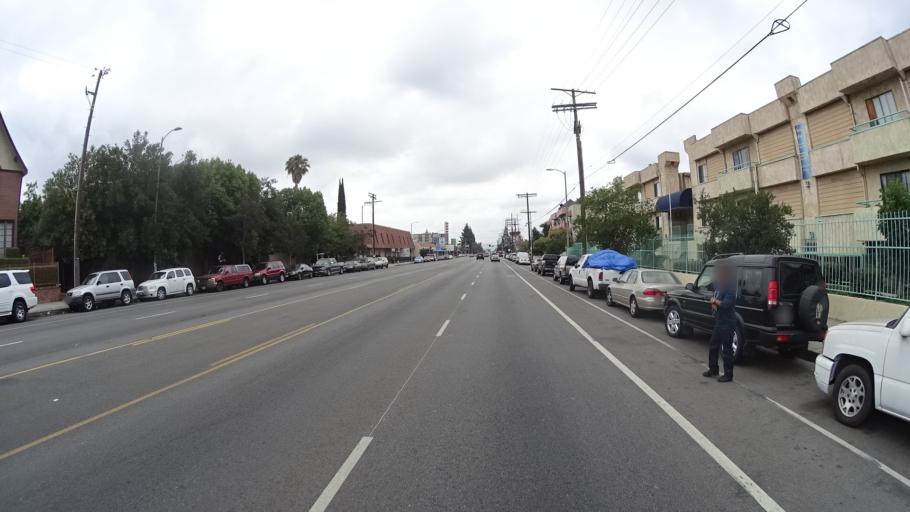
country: US
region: California
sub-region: Los Angeles County
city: San Fernando
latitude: 34.2377
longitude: -118.4503
